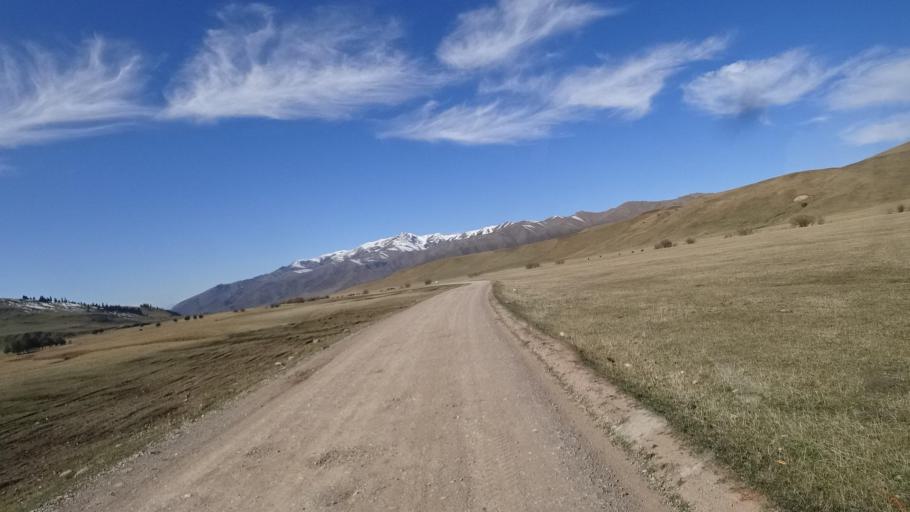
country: KZ
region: Almaty Oblysy
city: Kegen
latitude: 42.7300
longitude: 79.0402
